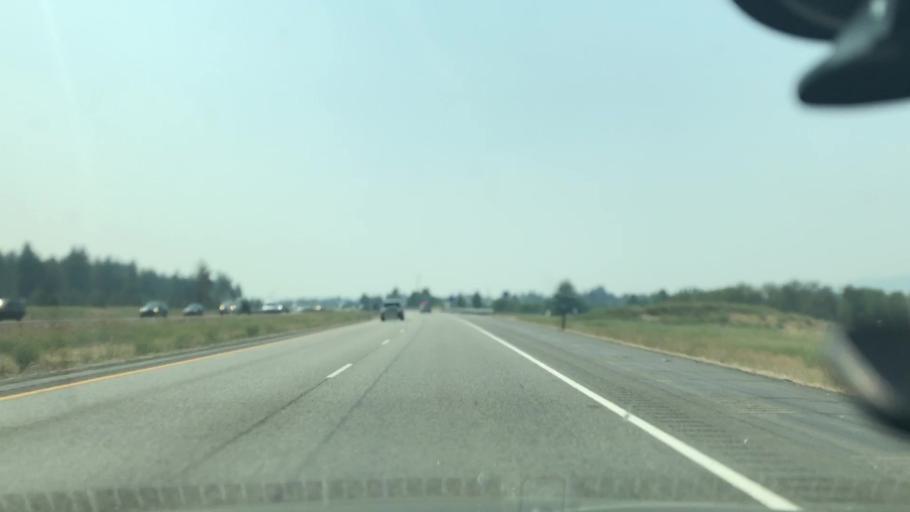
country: US
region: Washington
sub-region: Spokane County
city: Otis Orchards-East Farms
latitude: 47.6964
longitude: -117.0456
